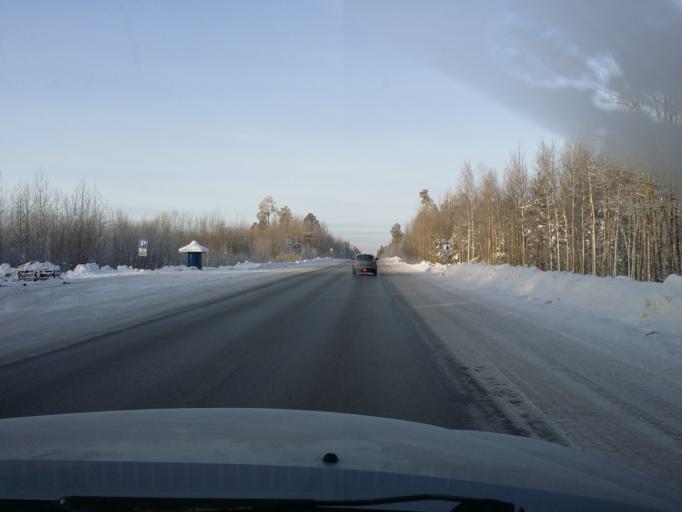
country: RU
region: Khanty-Mansiyskiy Avtonomnyy Okrug
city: Langepas
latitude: 61.2351
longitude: 75.2956
